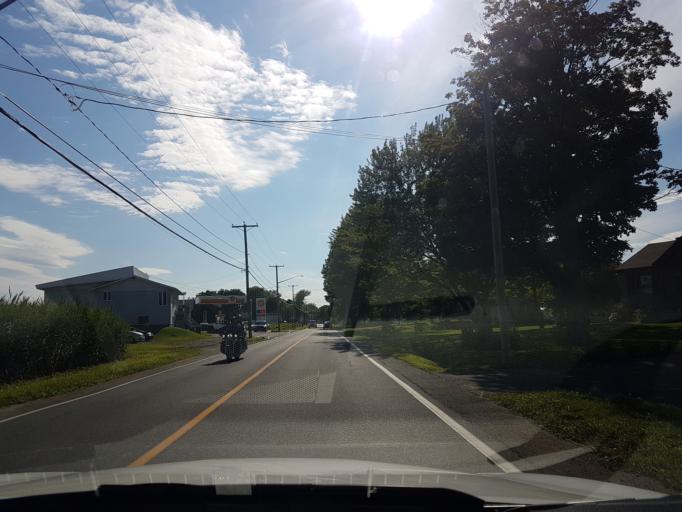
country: CA
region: Quebec
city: Sainte-Catherine
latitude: 46.2983
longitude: -72.6113
